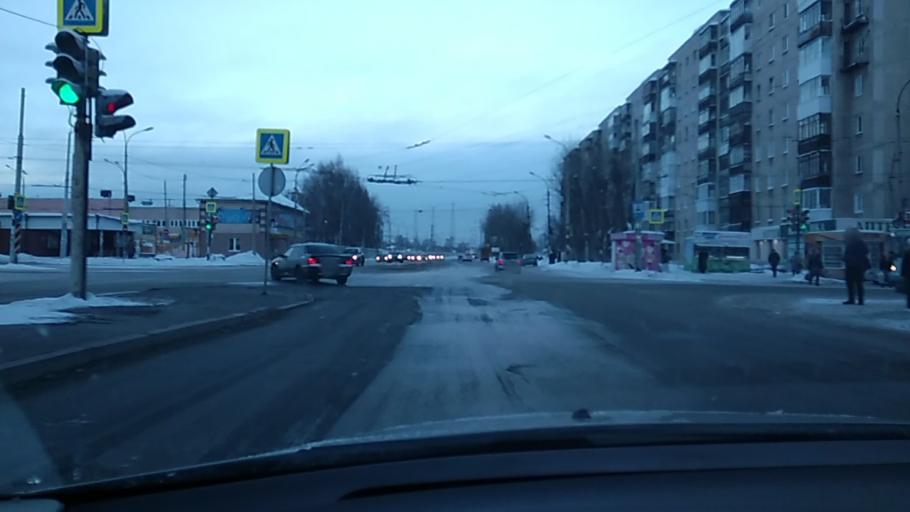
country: RU
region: Sverdlovsk
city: Yekaterinburg
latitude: 56.9091
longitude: 60.5927
